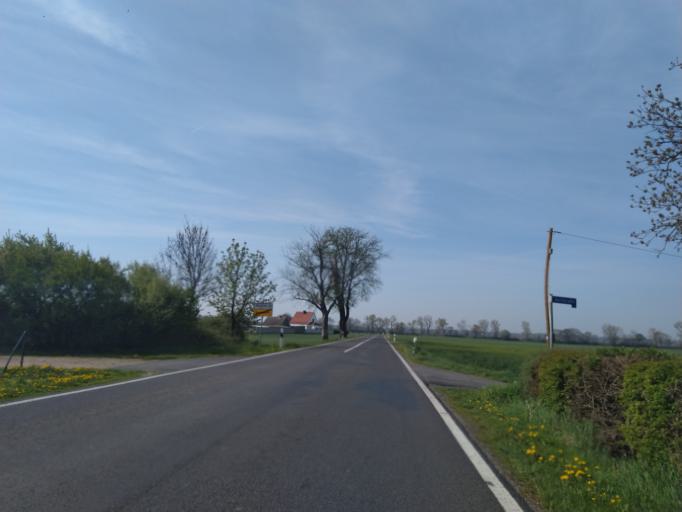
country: DE
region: Brandenburg
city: Wriezen
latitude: 52.7346
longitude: 14.1692
